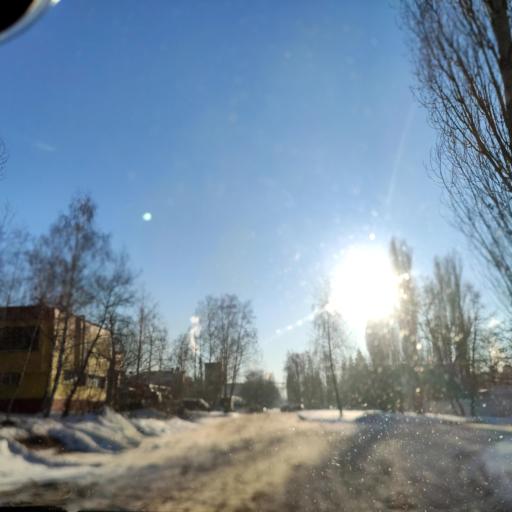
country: RU
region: Voronezj
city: Pridonskoy
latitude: 51.6750
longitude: 39.0937
